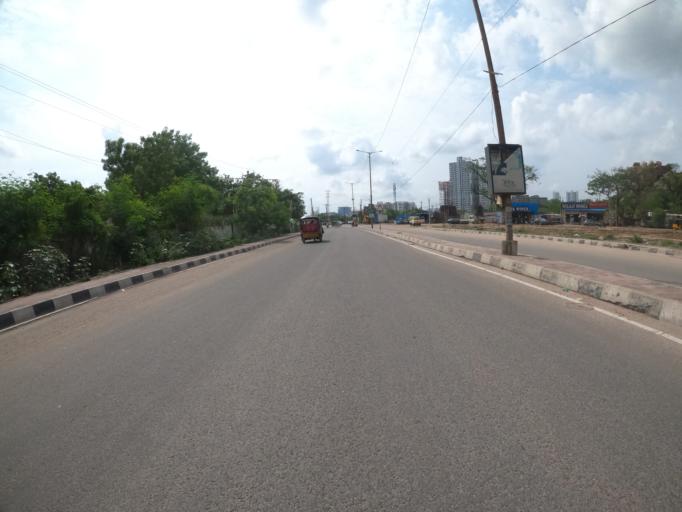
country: IN
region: Telangana
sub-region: Hyderabad
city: Hyderabad
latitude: 17.3874
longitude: 78.3456
